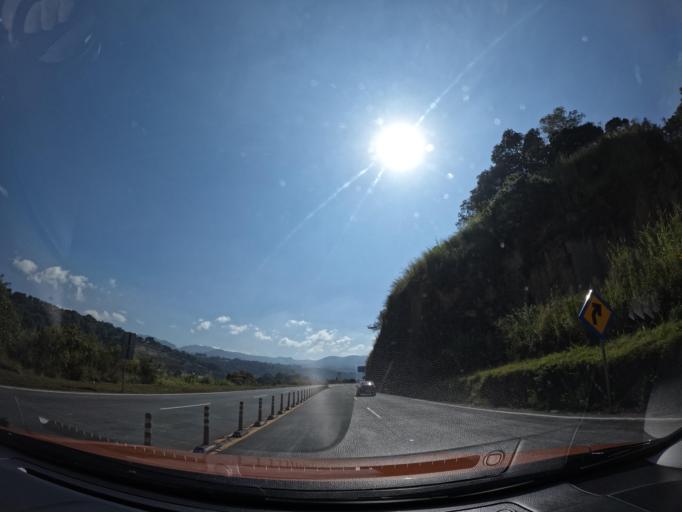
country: GT
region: Guatemala
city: Petapa
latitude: 14.4927
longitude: -90.5418
